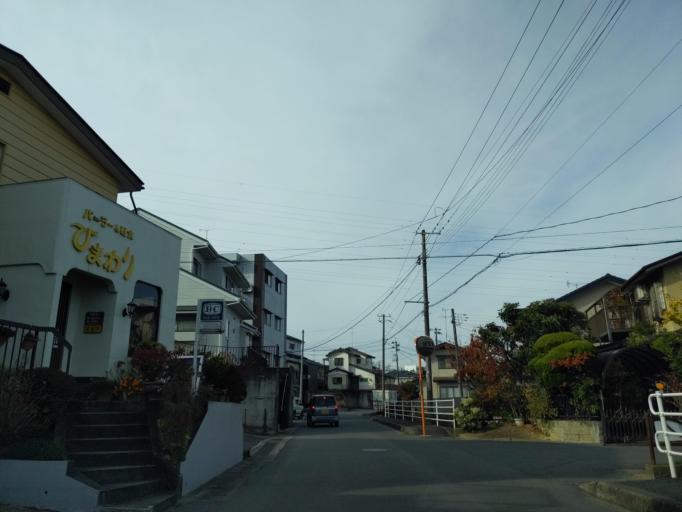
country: JP
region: Fukushima
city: Koriyama
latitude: 37.4159
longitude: 140.3795
